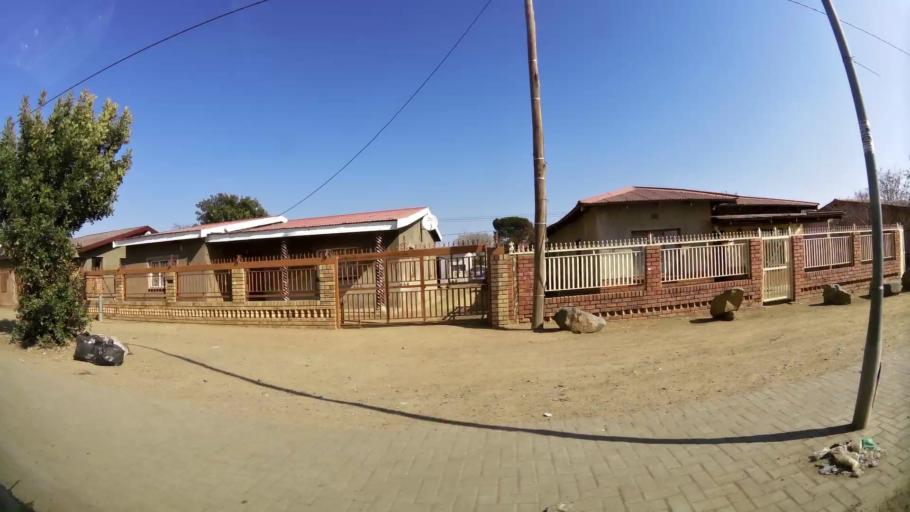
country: ZA
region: Orange Free State
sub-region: Mangaung Metropolitan Municipality
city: Bloemfontein
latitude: -29.1518
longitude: 26.2405
